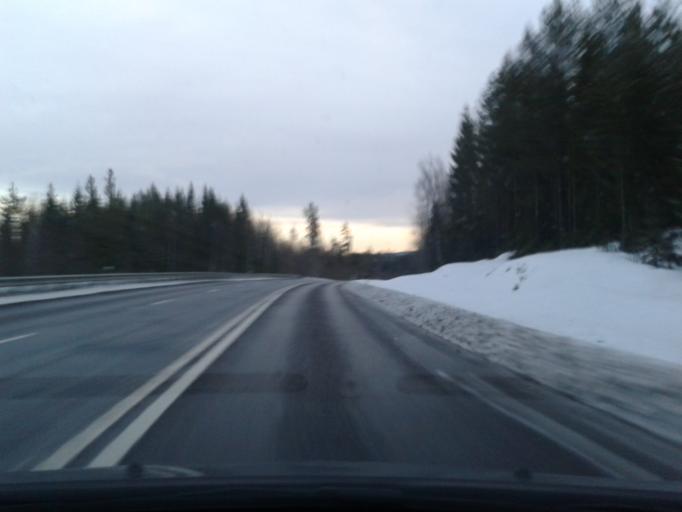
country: SE
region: Vaesternorrland
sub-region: Kramfors Kommun
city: Bollstabruk
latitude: 63.1061
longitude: 17.5078
